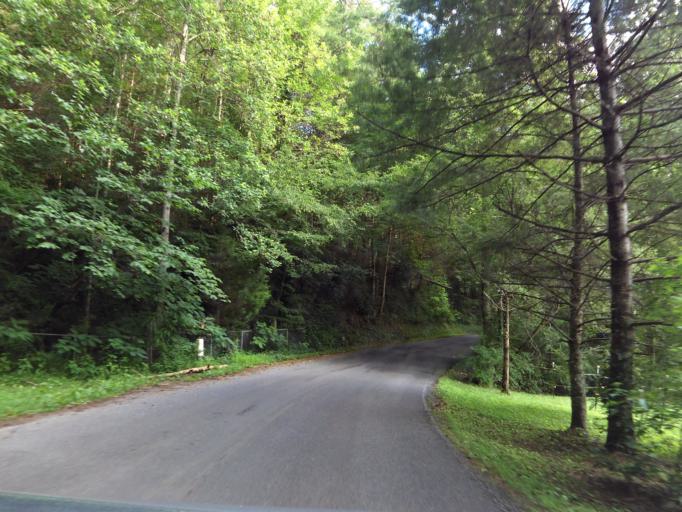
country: US
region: Tennessee
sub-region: Blount County
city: Maryville
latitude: 35.6145
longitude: -83.9425
